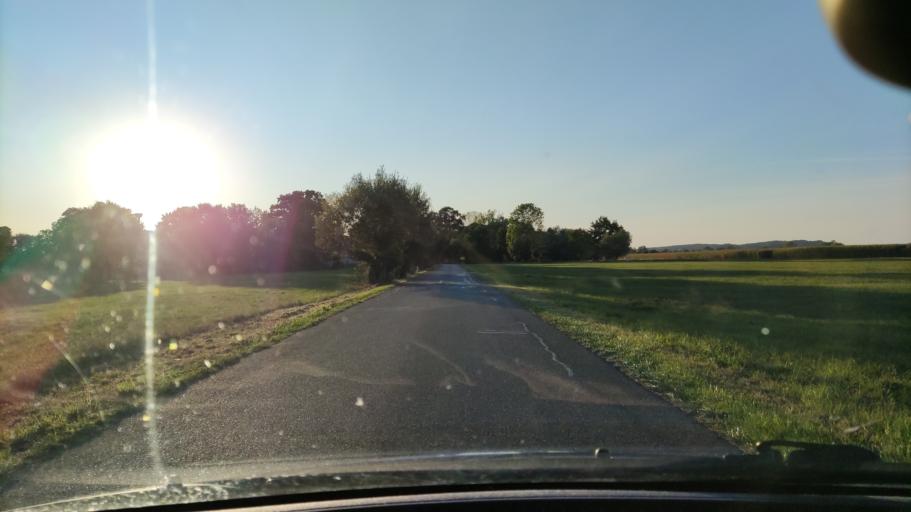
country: DE
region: Lower Saxony
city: Dannenberg
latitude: 53.1286
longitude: 11.0878
